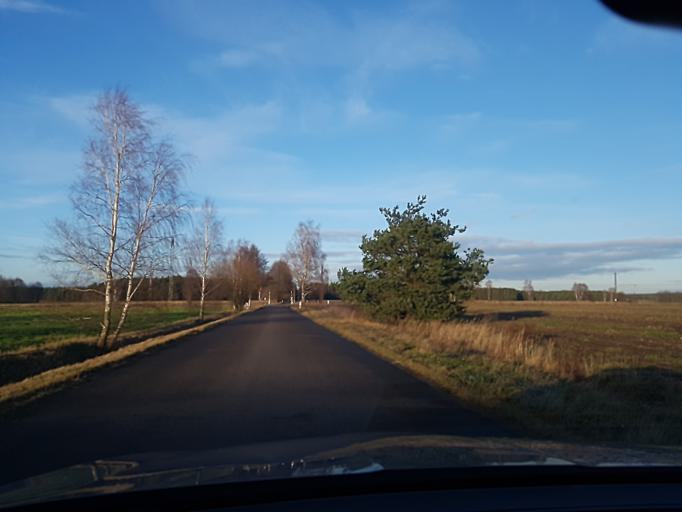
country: DE
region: Brandenburg
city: Schilda
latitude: 51.5906
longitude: 13.3850
